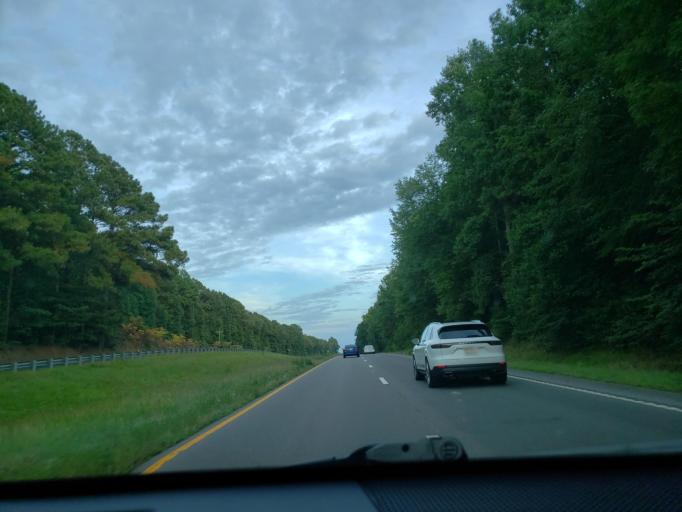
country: US
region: Virginia
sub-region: City of Emporia
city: Emporia
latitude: 36.7302
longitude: -77.6060
